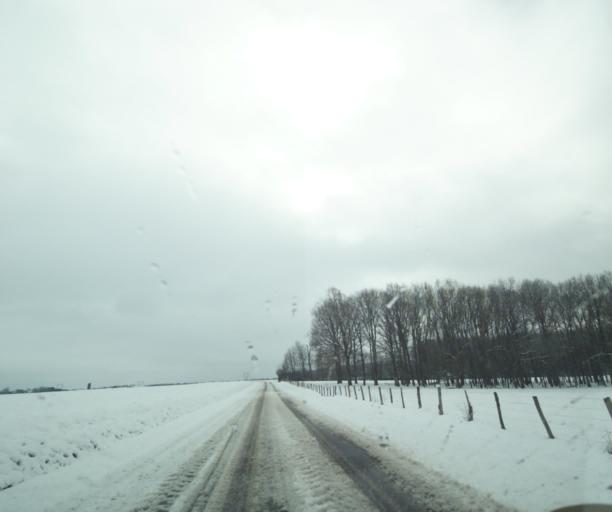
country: FR
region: Champagne-Ardenne
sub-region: Departement de la Haute-Marne
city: Montier-en-Der
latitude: 48.5172
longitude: 4.6799
